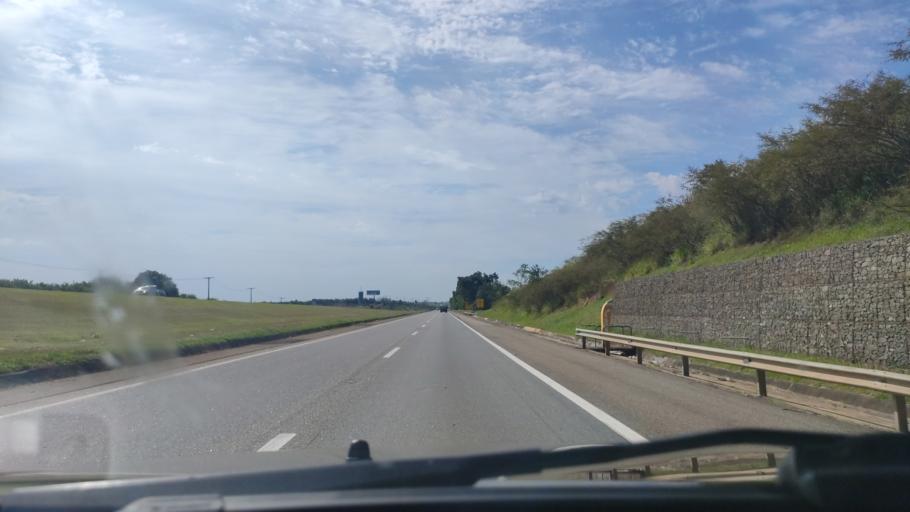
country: BR
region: Sao Paulo
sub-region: Boituva
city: Boituva
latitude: -23.3199
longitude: -47.5898
